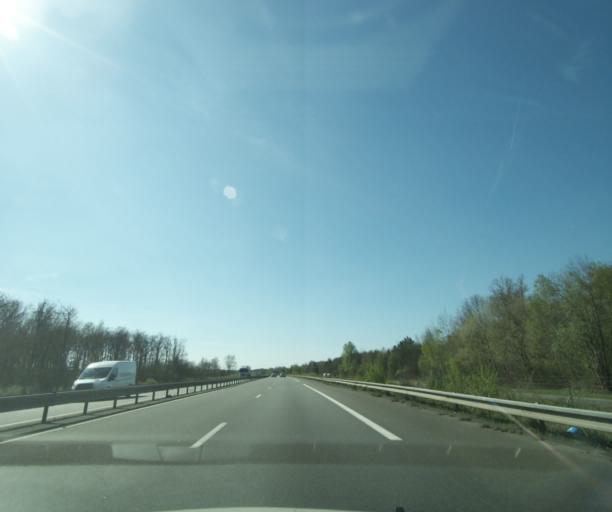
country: FR
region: Centre
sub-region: Departement du Loir-et-Cher
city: Theillay
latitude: 47.3386
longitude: 2.0475
